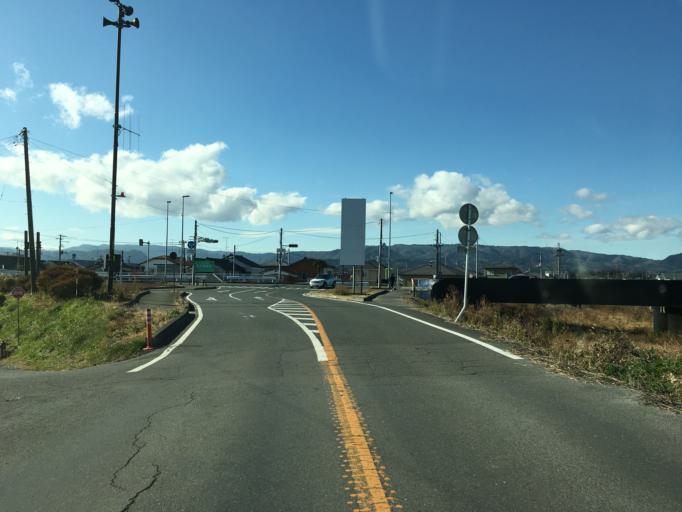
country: JP
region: Miyagi
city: Marumori
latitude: 37.7955
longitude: 140.9295
